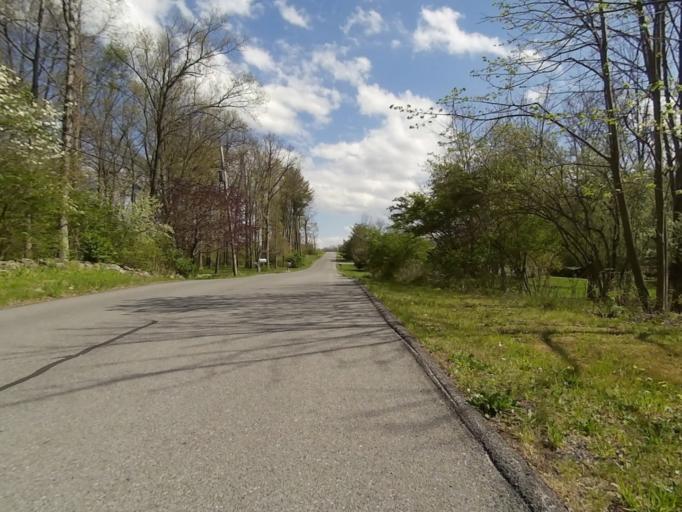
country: US
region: Pennsylvania
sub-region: Centre County
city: Bellefonte
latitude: 40.8840
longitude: -77.8243
